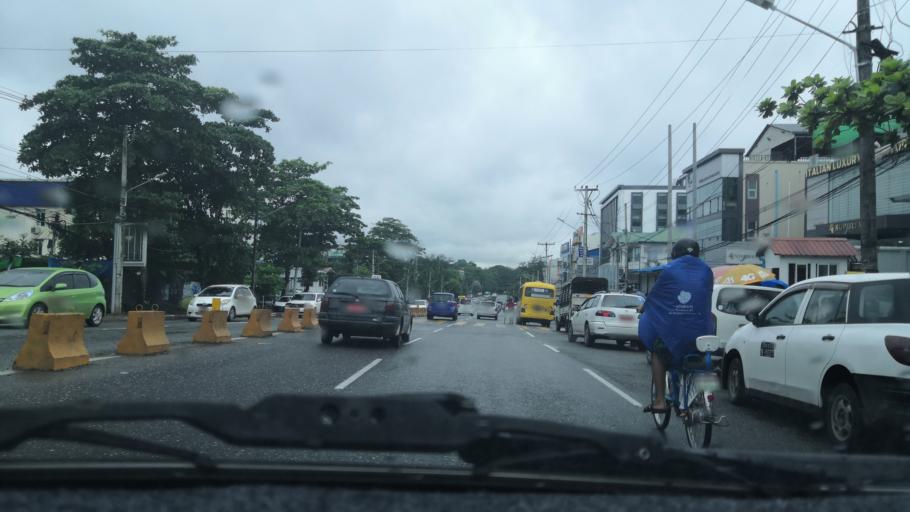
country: MM
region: Yangon
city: Yangon
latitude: 16.8888
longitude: 96.1293
